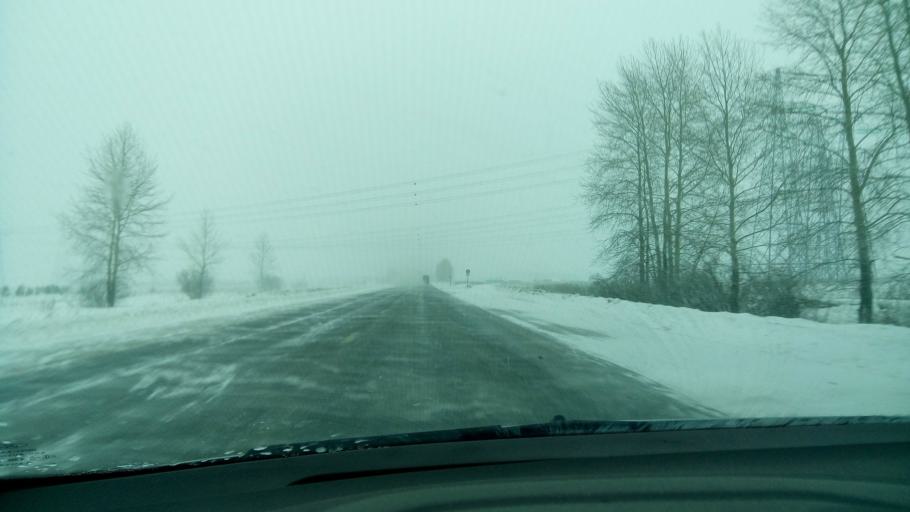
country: RU
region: Sverdlovsk
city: Beloyarskiy
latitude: 56.7740
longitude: 61.5156
